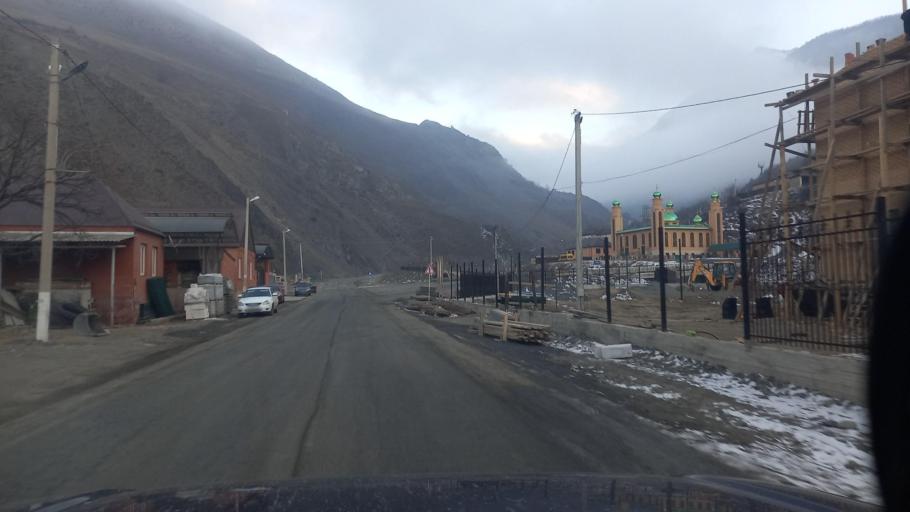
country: RU
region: Ingushetiya
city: Dzhayrakh
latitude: 42.8022
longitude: 44.7550
